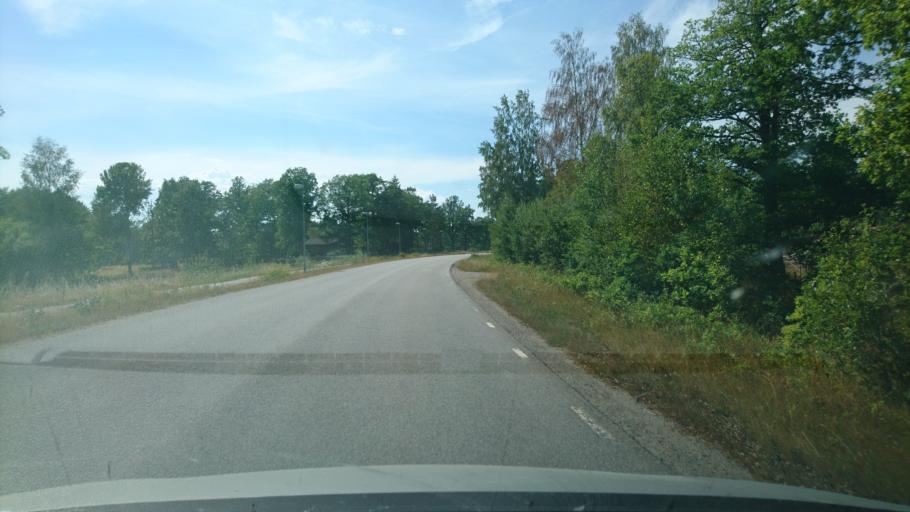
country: SE
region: Kalmar
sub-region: Vasterviks Kommun
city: Vaestervik
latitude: 57.7671
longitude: 16.6659
